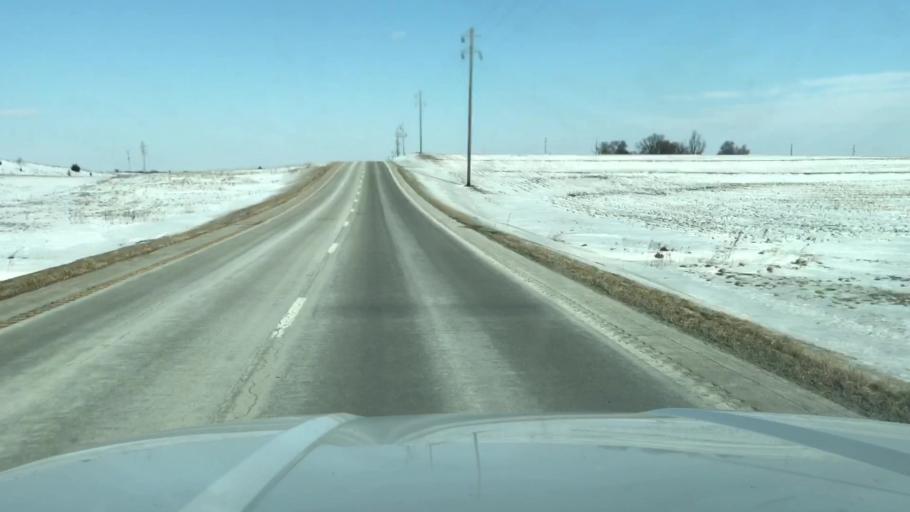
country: US
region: Missouri
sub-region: Andrew County
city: Savannah
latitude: 40.1247
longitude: -94.8695
